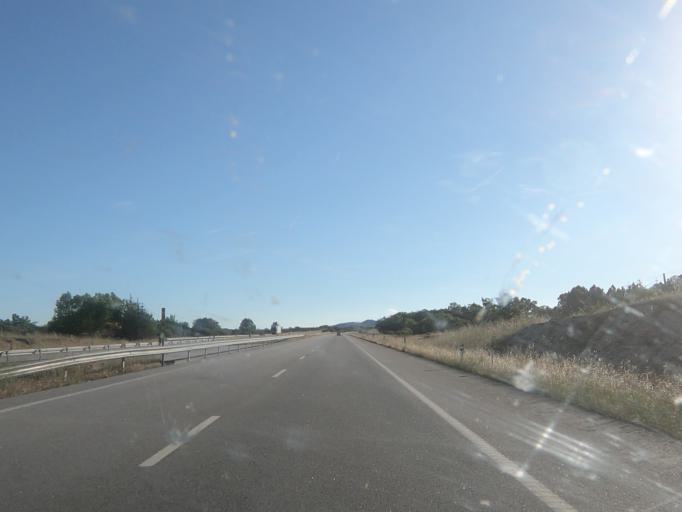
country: PT
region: Guarda
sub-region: Guarda
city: Sequeira
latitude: 40.6036
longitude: -7.0837
